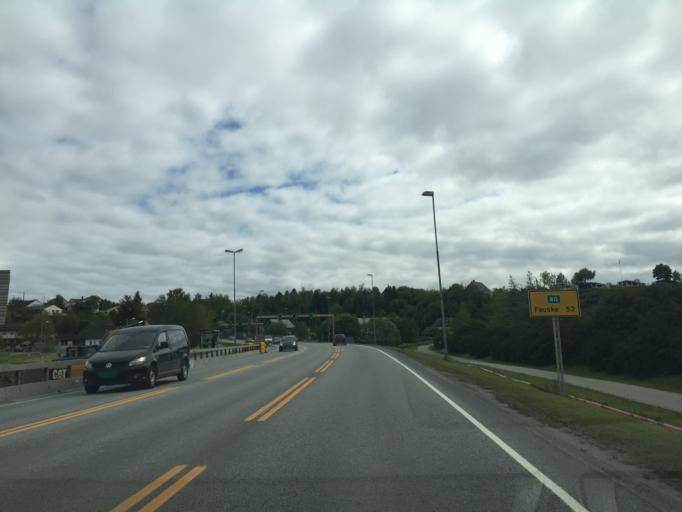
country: NO
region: Nordland
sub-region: Bodo
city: Bodo
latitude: 67.2765
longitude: 14.4385
